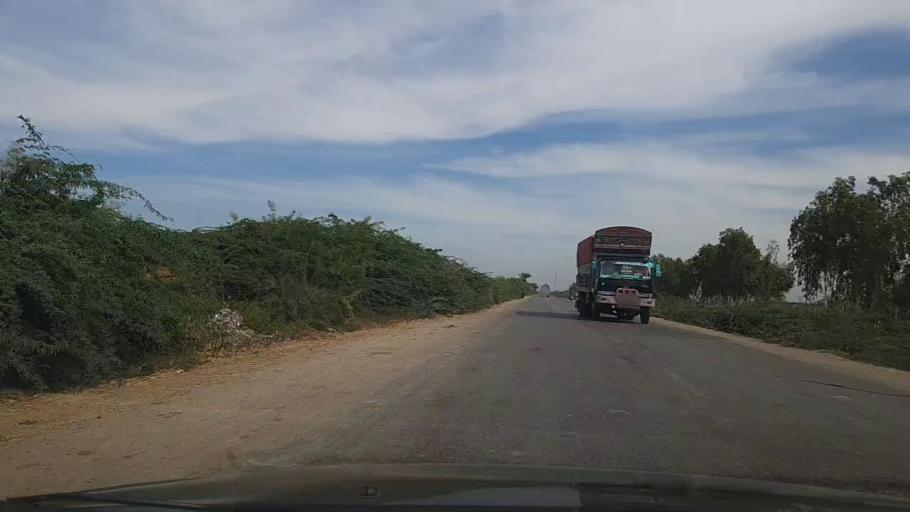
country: PK
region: Sindh
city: Thatta
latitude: 24.8002
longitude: 67.9650
